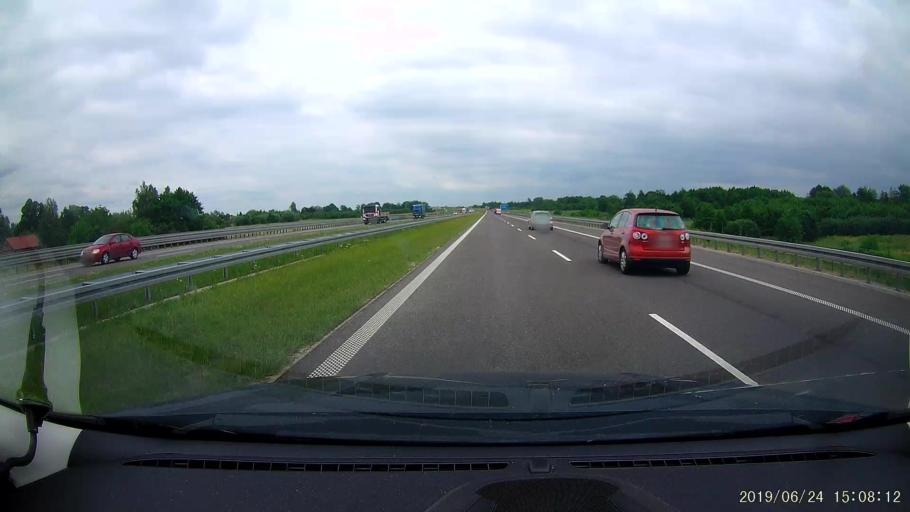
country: PL
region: Subcarpathian Voivodeship
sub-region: Powiat lancucki
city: Czarna
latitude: 50.0915
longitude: 22.1920
